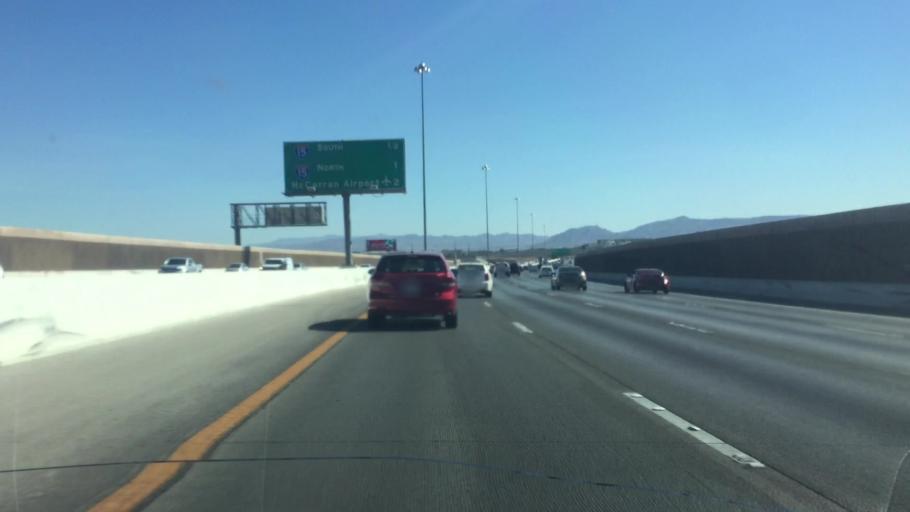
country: US
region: Nevada
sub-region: Clark County
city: Paradise
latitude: 36.0684
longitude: -115.1973
